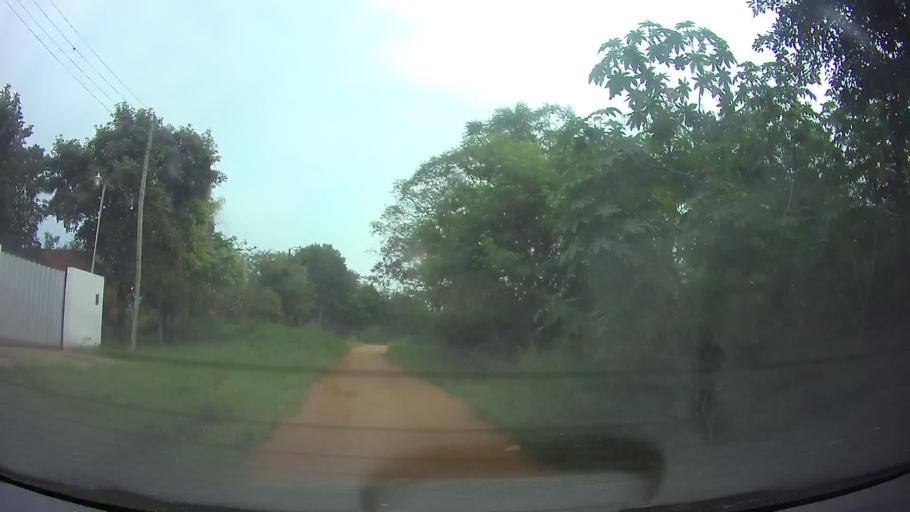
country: PY
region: Central
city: Limpio
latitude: -25.2376
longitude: -57.4582
